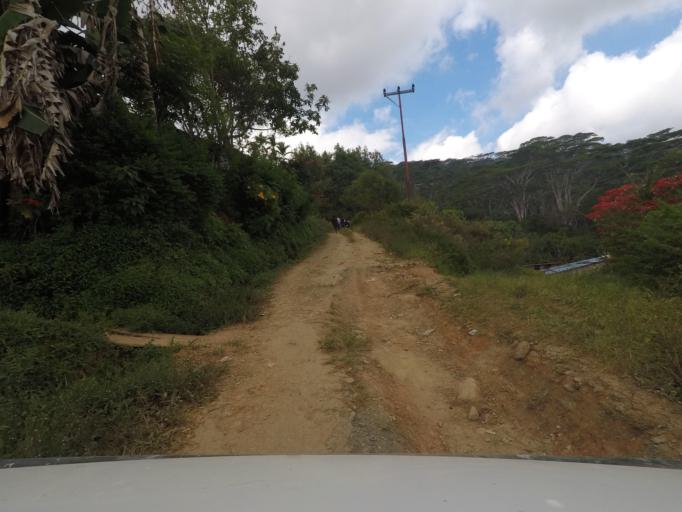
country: TL
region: Ermera
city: Gleno
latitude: -8.7225
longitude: 125.3250
